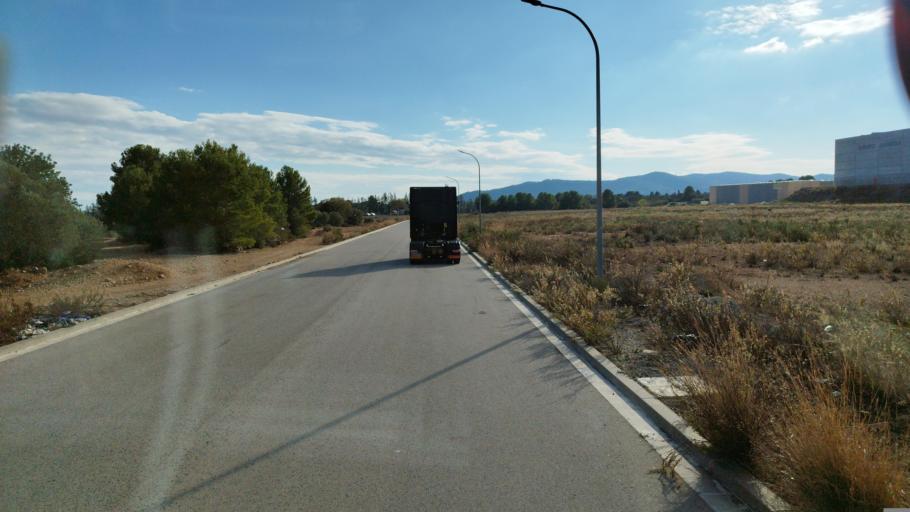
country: ES
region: Catalonia
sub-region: Provincia de Tarragona
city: Santa Oliva
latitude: 41.2721
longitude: 1.5237
